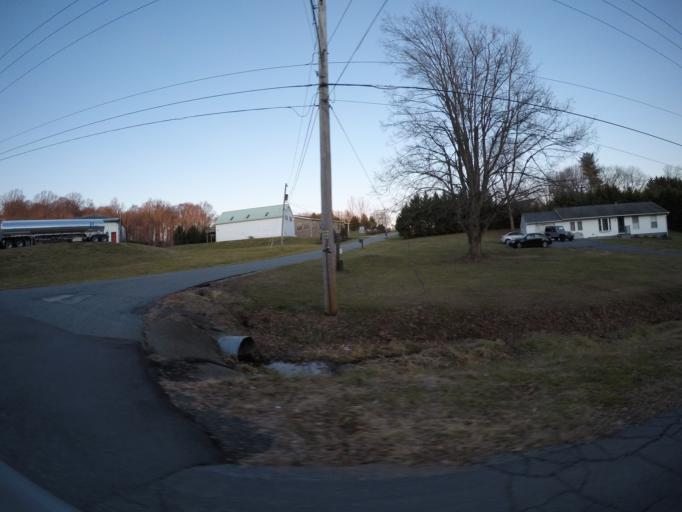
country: US
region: Maryland
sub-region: Cecil County
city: Rising Sun
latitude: 39.7077
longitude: -76.0649
